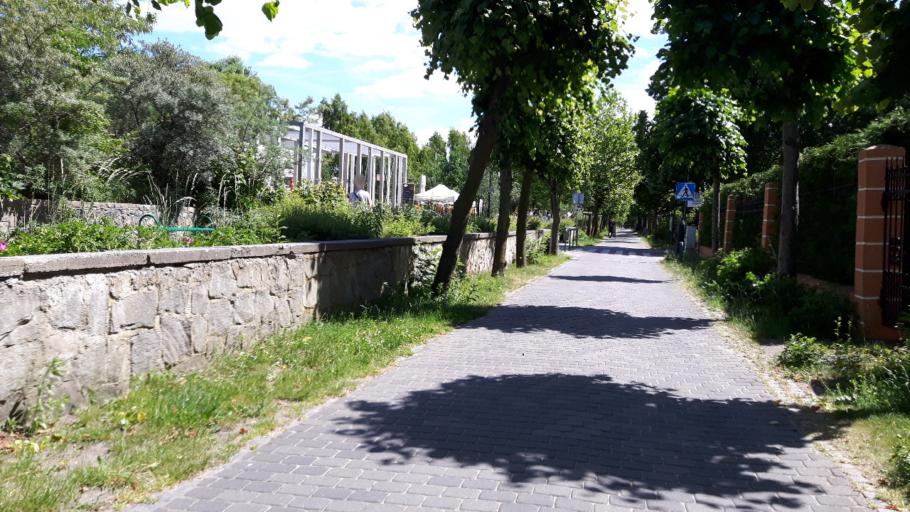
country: PL
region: Pomeranian Voivodeship
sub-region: Sopot
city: Sopot
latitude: 54.4406
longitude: 18.5760
